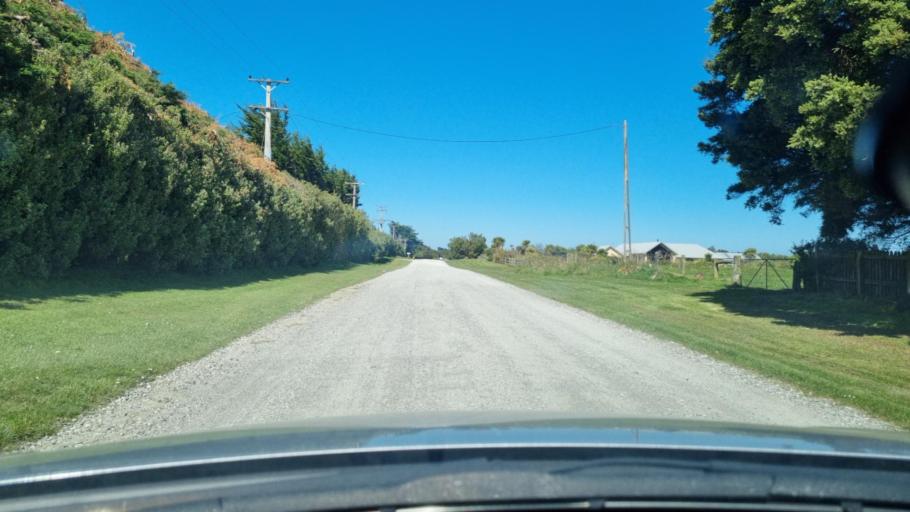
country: NZ
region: Southland
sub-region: Invercargill City
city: Invercargill
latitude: -46.4421
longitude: 168.2784
